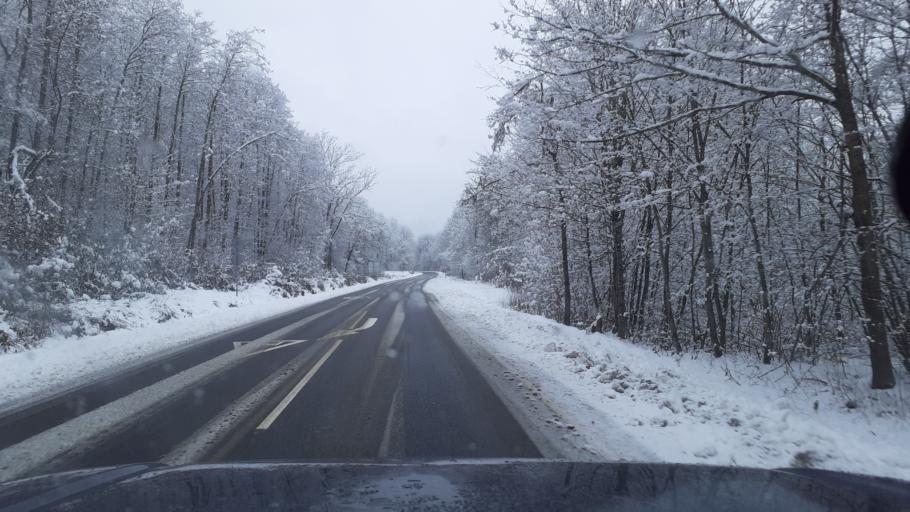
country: RU
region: Adygeya
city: Kamennomostskiy
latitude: 44.1900
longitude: 40.1673
